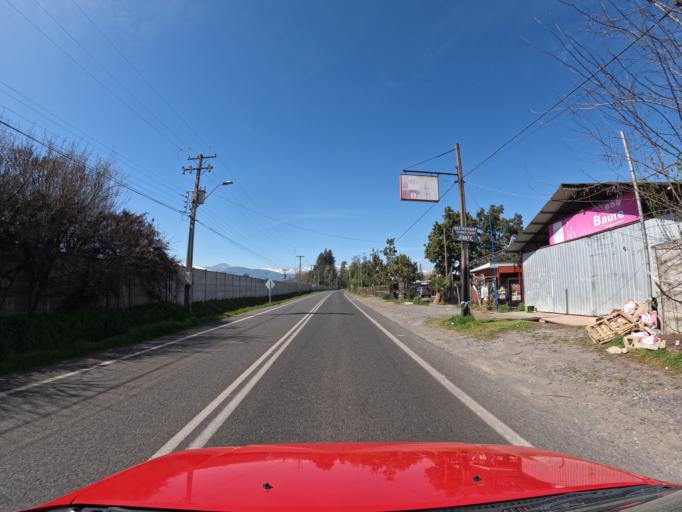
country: CL
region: Maule
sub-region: Provincia de Curico
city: Teno
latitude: -34.9693
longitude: -71.0196
